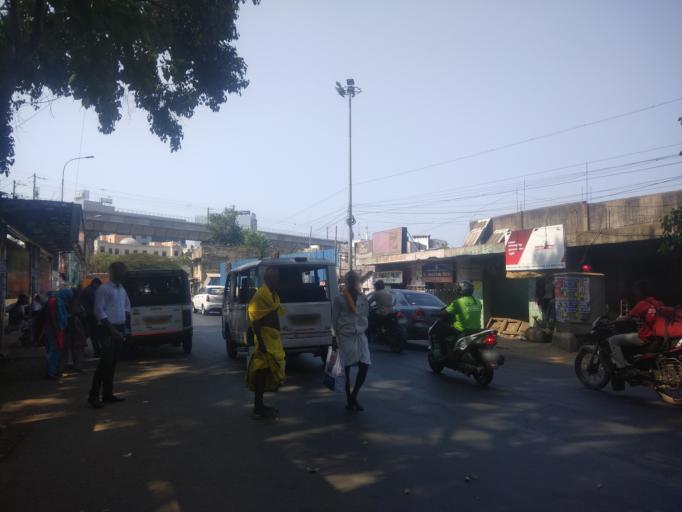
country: IN
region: Tamil Nadu
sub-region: Kancheepuram
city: Alandur
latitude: 13.0072
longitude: 80.2098
